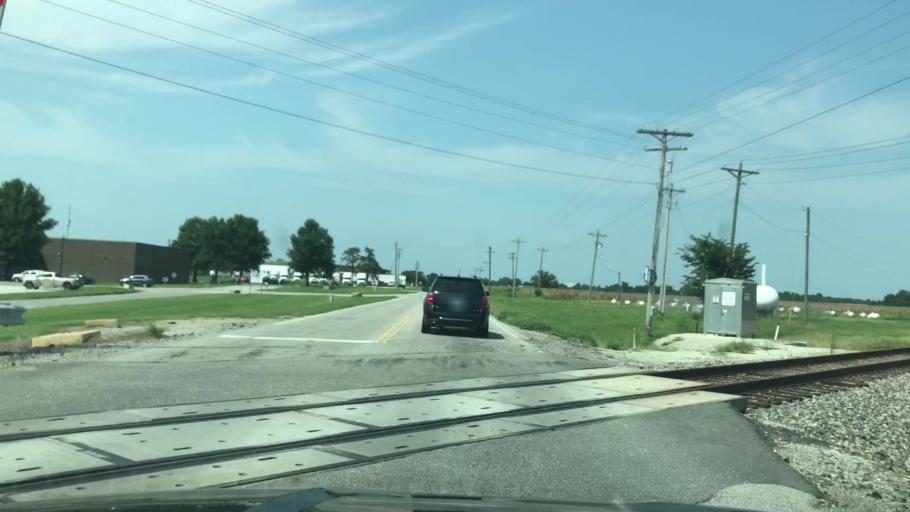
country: US
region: Oklahoma
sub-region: Ottawa County
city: Commerce
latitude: 36.9125
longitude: -94.8419
